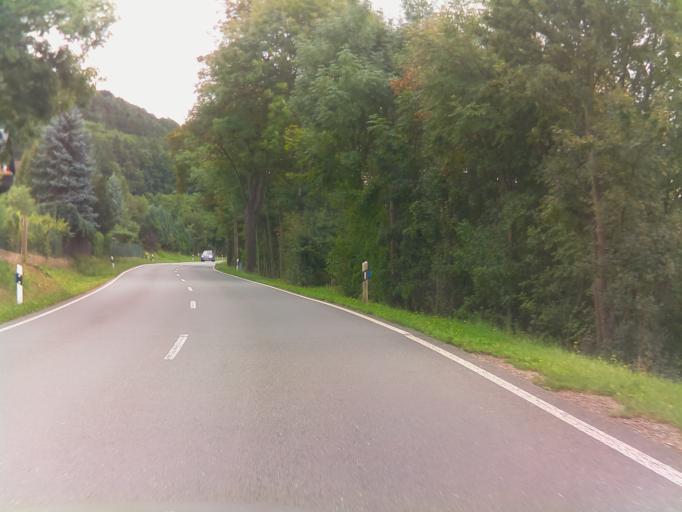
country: DE
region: Thuringia
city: Saalfeld
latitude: 50.6256
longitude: 11.3825
